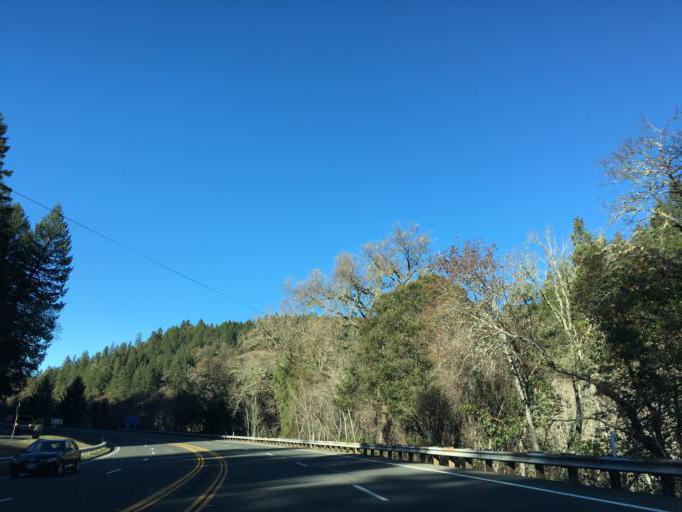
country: US
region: California
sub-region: Mendocino County
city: Brooktrails
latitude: 39.5501
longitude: -123.4247
